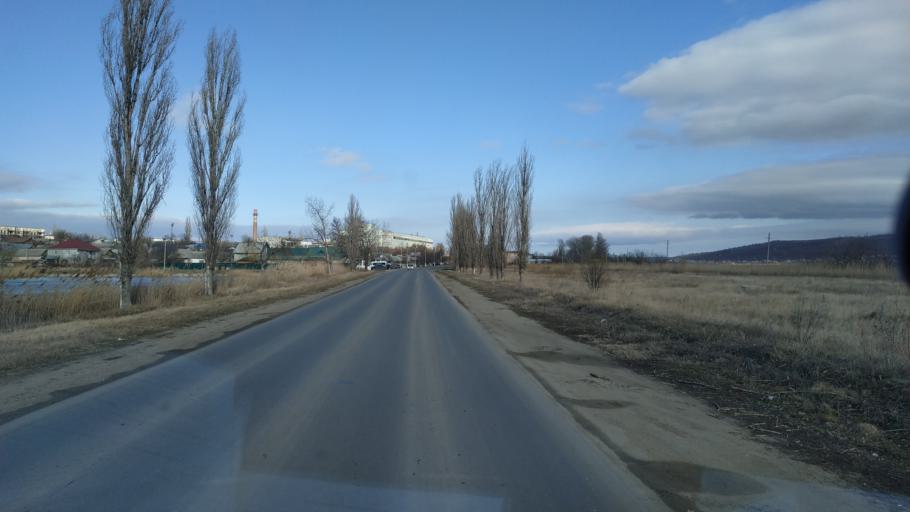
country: MD
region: Causeni
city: Causeni
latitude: 46.6548
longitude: 29.4132
